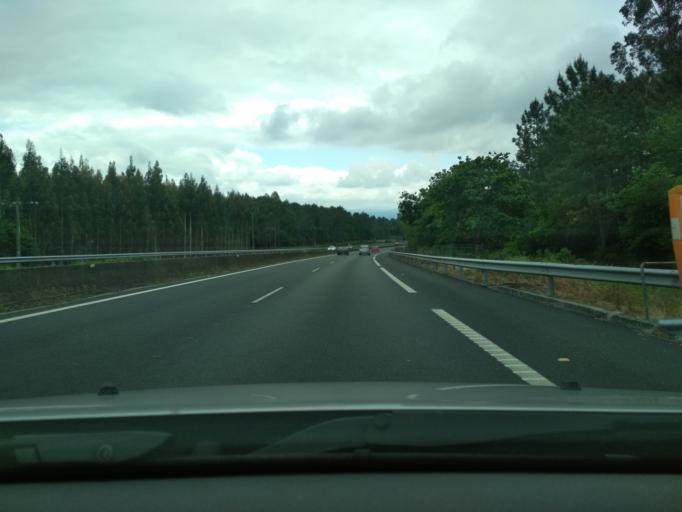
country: ES
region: Galicia
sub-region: Provincia da Coruna
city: Santiago de Compostela
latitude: 42.8250
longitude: -8.5710
